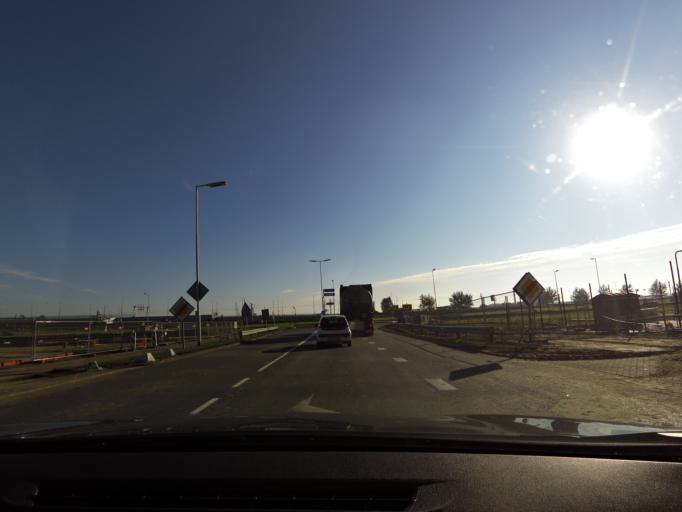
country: NL
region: South Holland
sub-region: Gemeente Spijkenisse
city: Spijkenisse
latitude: 51.8722
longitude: 4.3245
